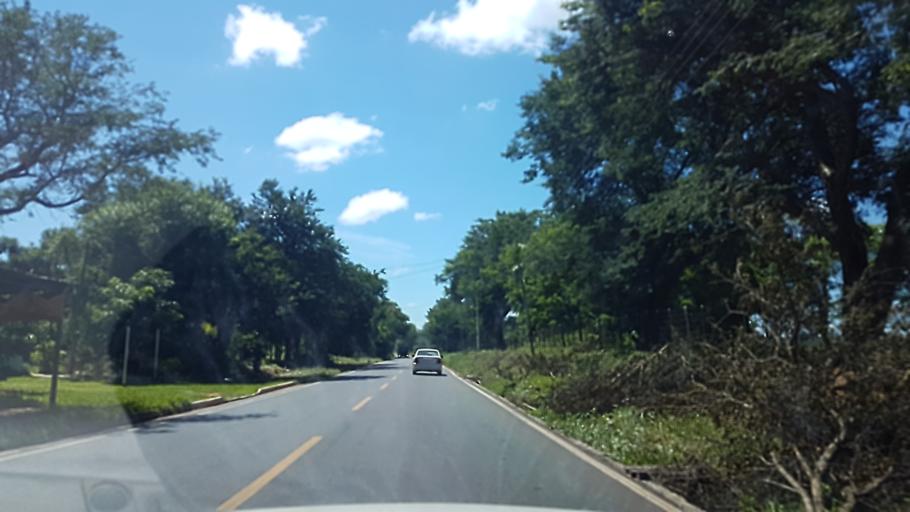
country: PY
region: Central
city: Capiata
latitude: -25.3136
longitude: -57.4637
